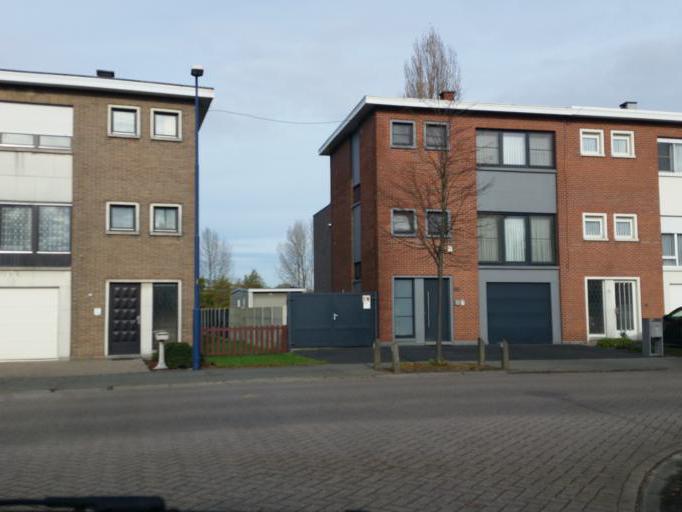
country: BE
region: Flanders
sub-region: Provincie Antwerpen
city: Kontich
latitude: 51.1431
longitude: 4.4493
